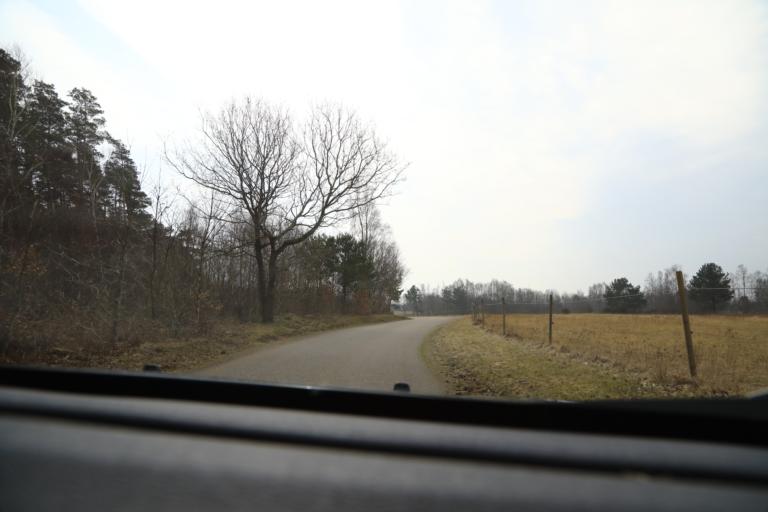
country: SE
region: Halland
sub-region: Kungsbacka Kommun
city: Frillesas
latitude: 57.2702
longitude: 12.1376
